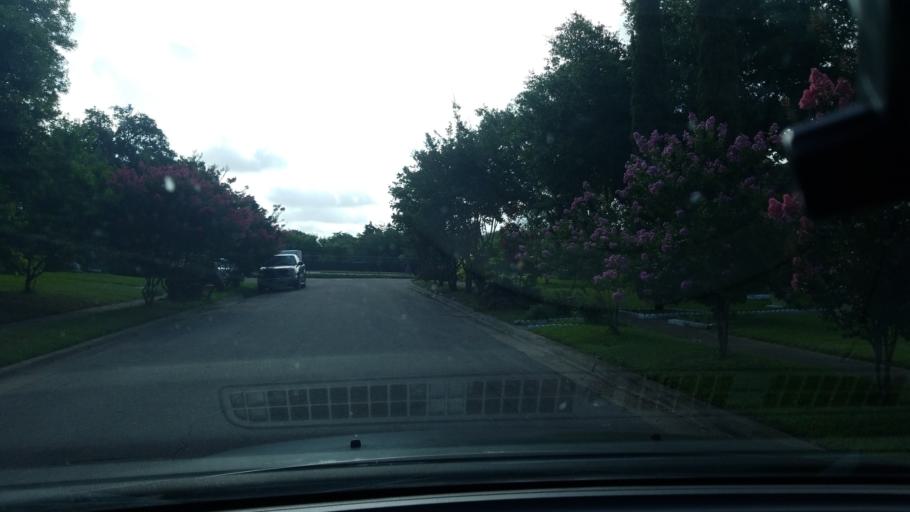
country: US
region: Texas
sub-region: Dallas County
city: Mesquite
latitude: 32.8141
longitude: -96.6830
